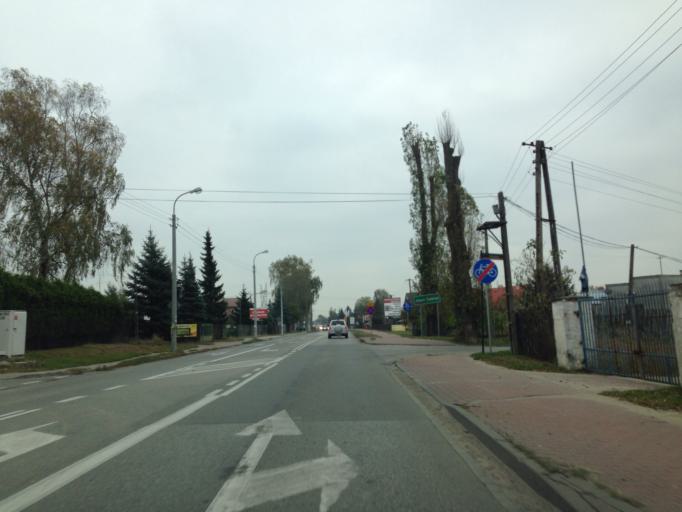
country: PL
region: Masovian Voivodeship
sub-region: Powiat warszawski zachodni
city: Stare Babice
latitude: 52.2514
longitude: 20.8226
